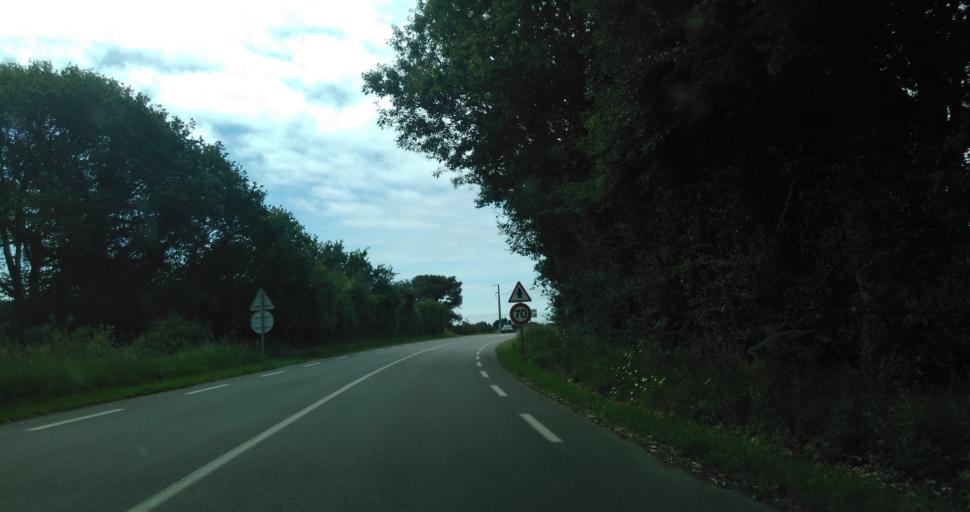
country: FR
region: Brittany
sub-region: Departement du Morbihan
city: La Trinite-sur-Mer
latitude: 47.6047
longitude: -3.0435
